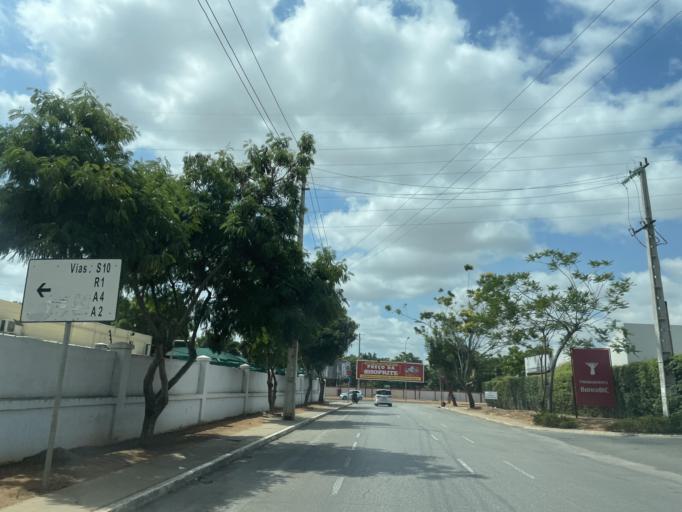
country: AO
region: Luanda
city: Luanda
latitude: -8.9232
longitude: 13.1808
